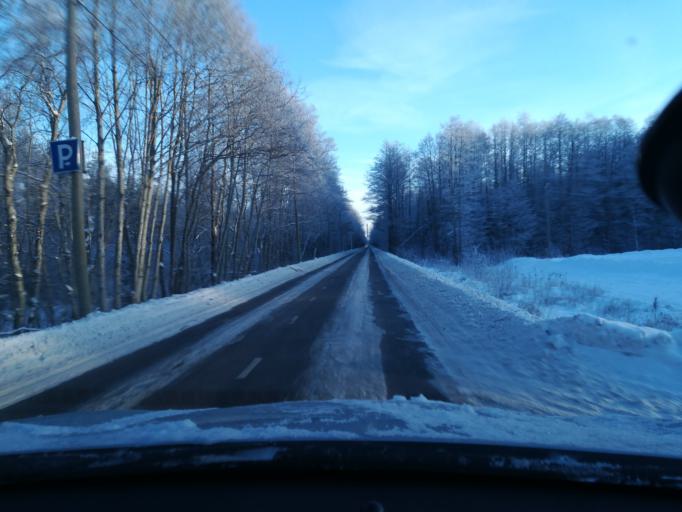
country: EE
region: Harju
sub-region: Saue vald
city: Laagri
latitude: 59.3904
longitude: 24.6138
